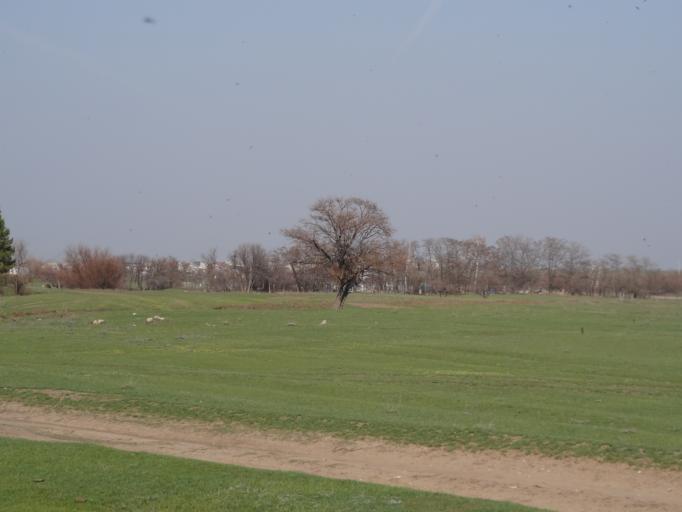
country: RU
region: Saratov
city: Privolzhskiy
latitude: 51.3189
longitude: 45.9730
